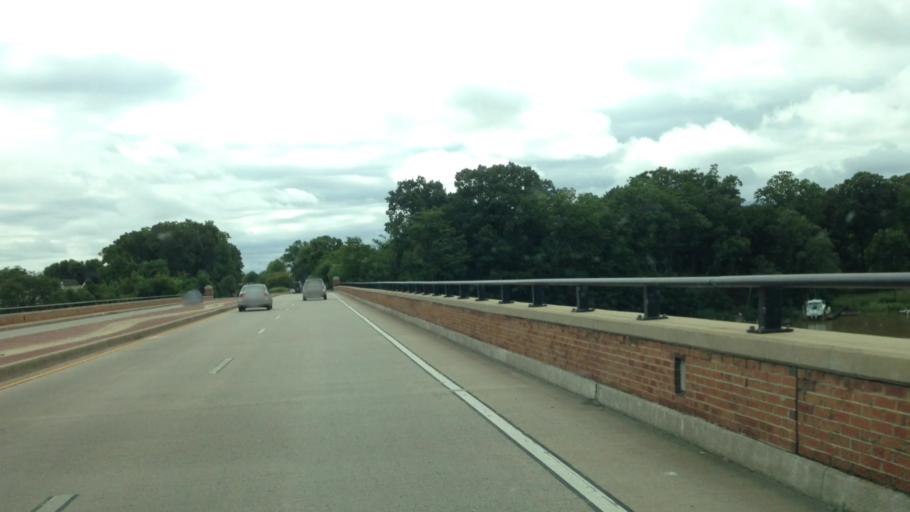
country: US
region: Maryland
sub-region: Anne Arundel County
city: Annapolis
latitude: 38.9916
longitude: -76.5099
